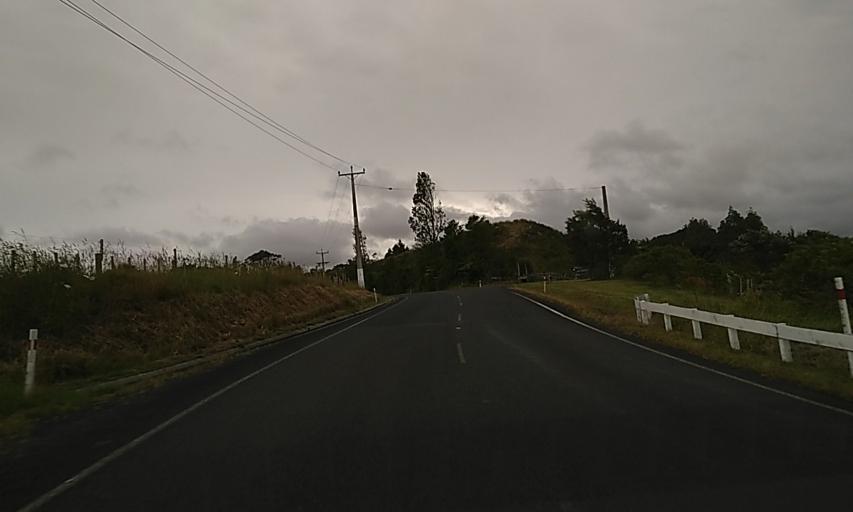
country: NZ
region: Auckland
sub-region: Auckland
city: Pukekohe East
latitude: -37.3154
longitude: 174.9382
